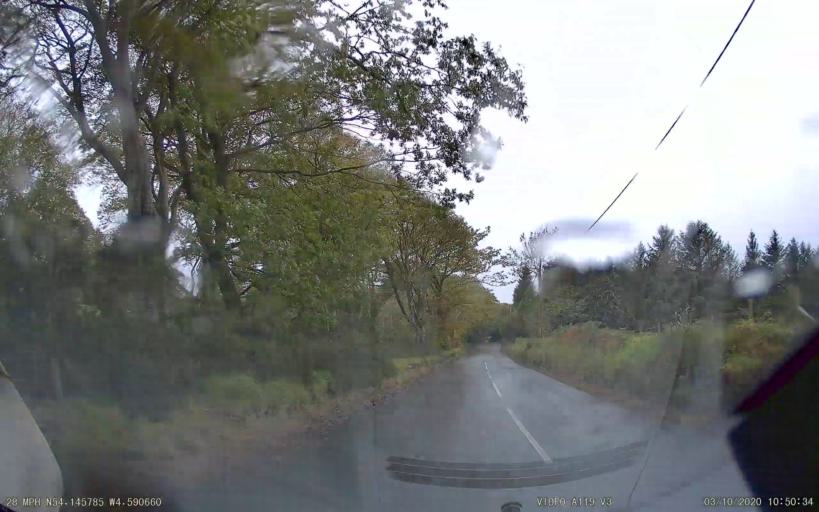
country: IM
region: Castletown
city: Castletown
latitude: 54.1458
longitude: -4.5907
